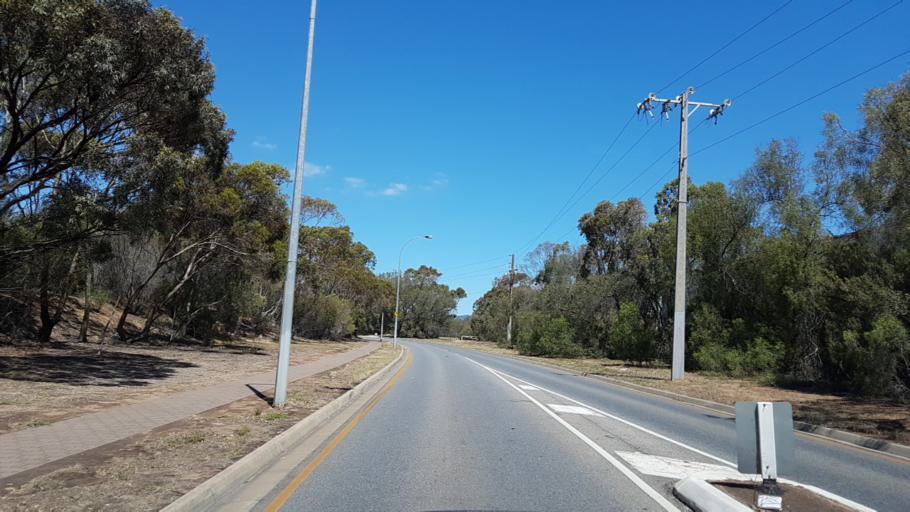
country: AU
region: South Australia
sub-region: Salisbury
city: Salisbury
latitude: -34.7924
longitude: 138.6039
